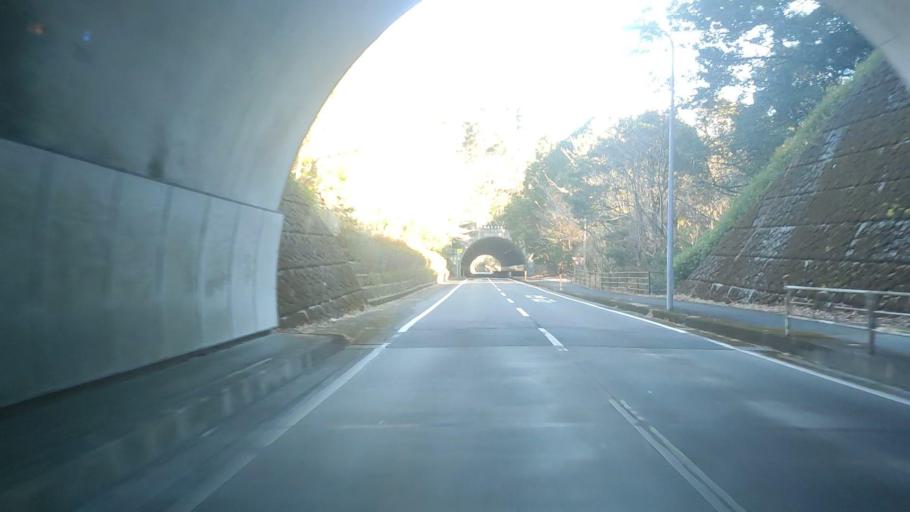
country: JP
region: Miyazaki
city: Nobeoka
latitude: 32.7007
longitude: 131.8150
